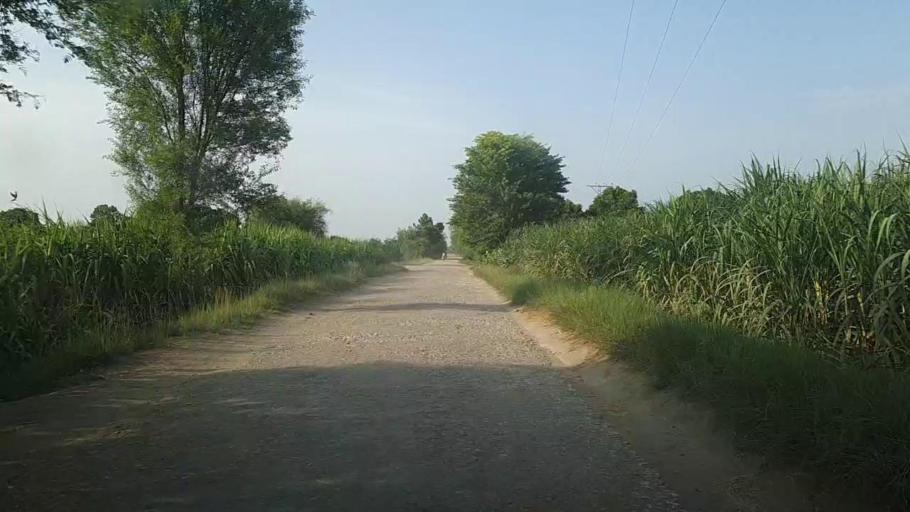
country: PK
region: Sindh
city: Ubauro
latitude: 28.3282
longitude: 69.7973
